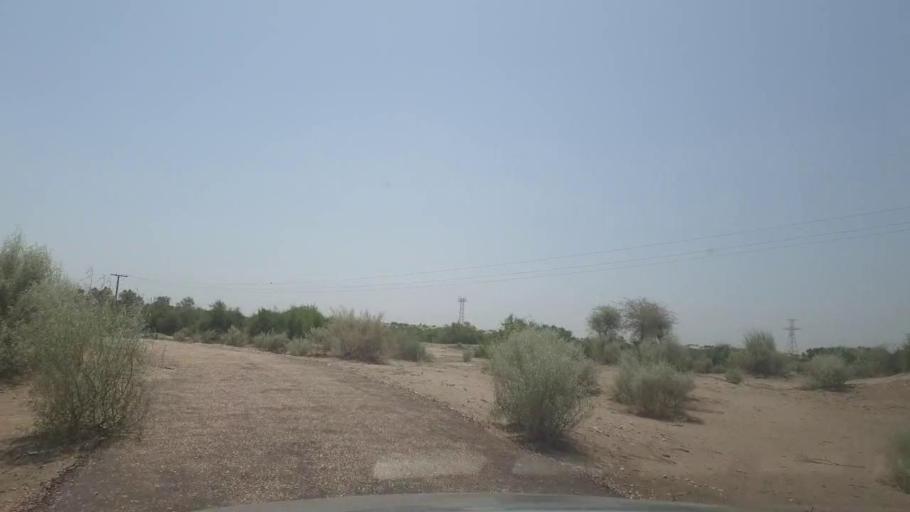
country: PK
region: Sindh
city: Khairpur
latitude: 27.3531
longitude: 69.0789
